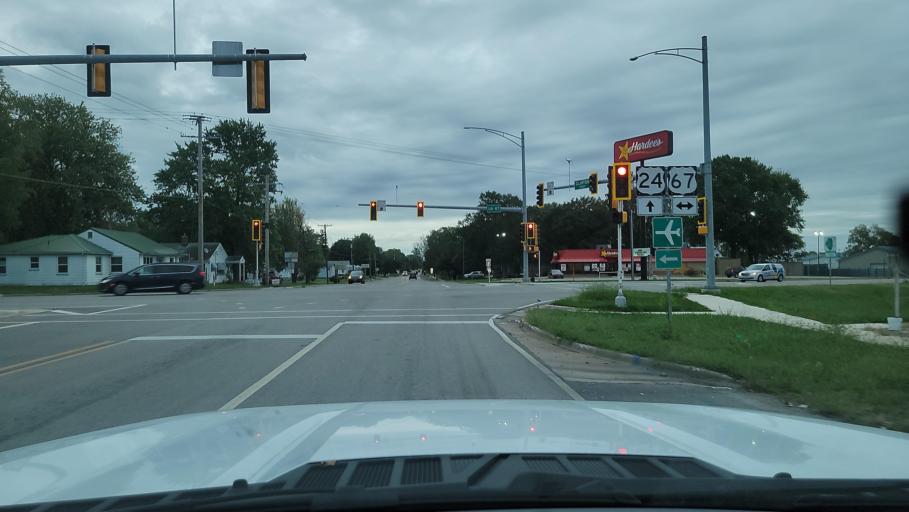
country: US
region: Illinois
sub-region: Schuyler County
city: Rushville
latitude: 40.1176
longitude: -90.5758
